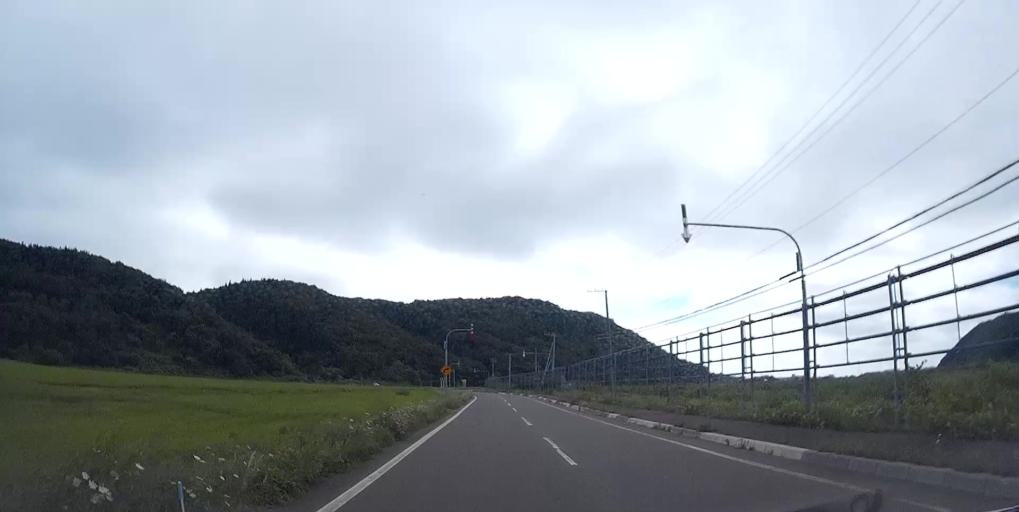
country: JP
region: Hokkaido
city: Kamiiso
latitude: 41.9732
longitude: 140.1576
